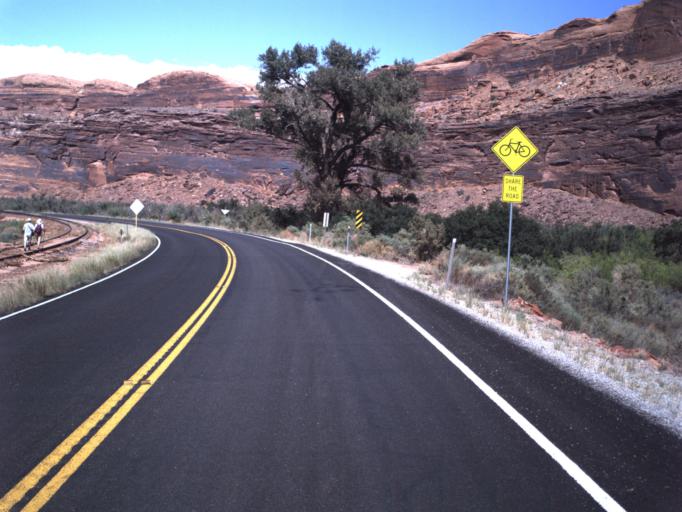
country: US
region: Utah
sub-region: Grand County
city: Moab
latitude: 38.5471
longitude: -109.6475
